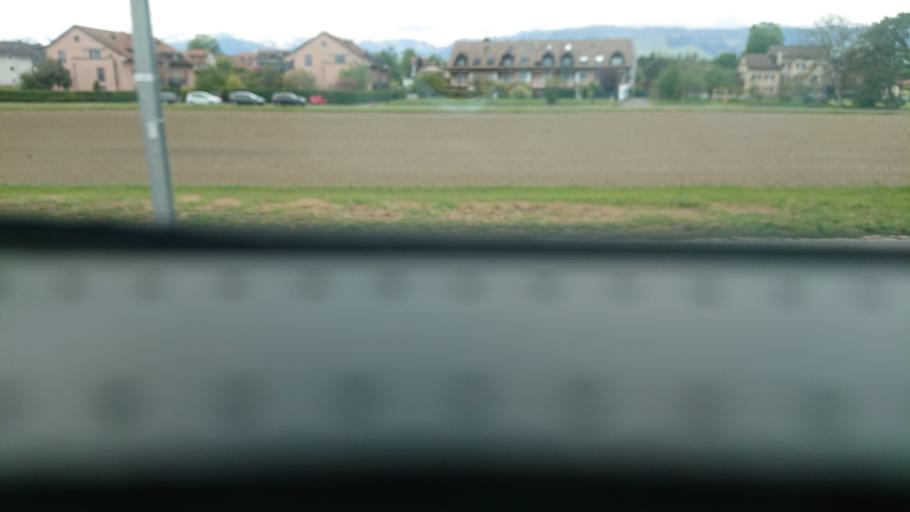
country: CH
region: Vaud
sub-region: Nyon District
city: Founex
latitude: 46.3316
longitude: 6.1961
